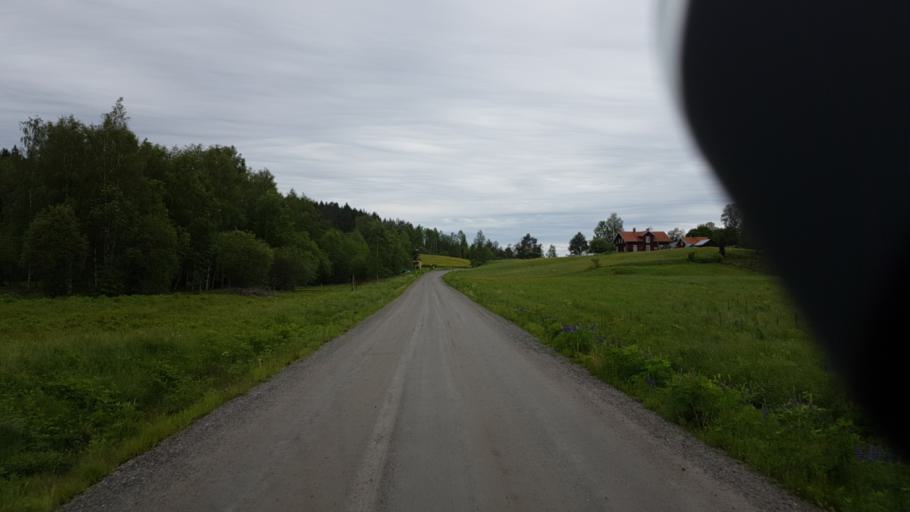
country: NO
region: Ostfold
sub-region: Romskog
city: Romskog
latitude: 59.6716
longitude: 11.9333
